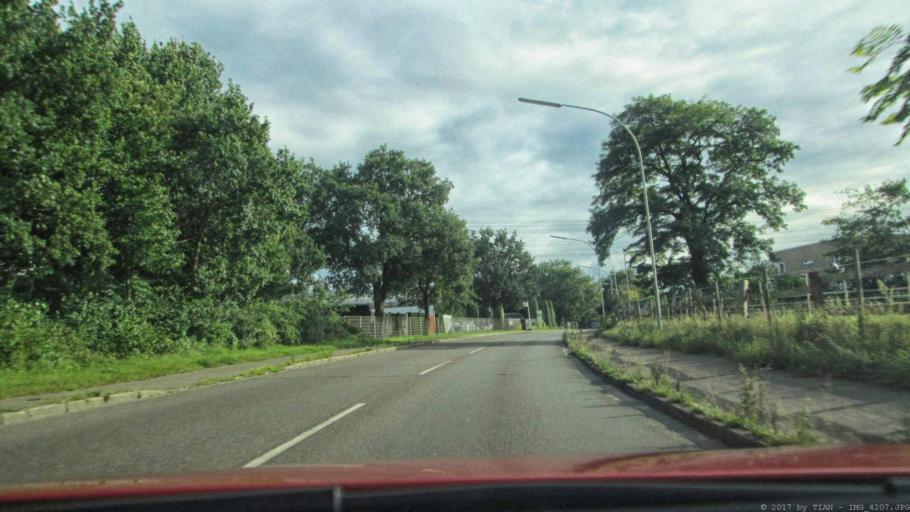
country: DE
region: Schleswig-Holstein
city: Halstenbek
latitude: 53.5890
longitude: 9.8240
